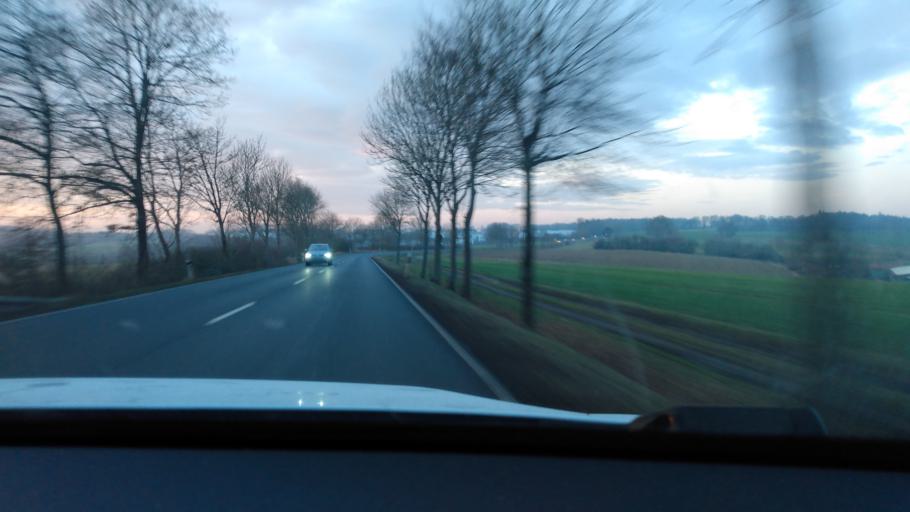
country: DE
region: Rheinland-Pfalz
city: Kircheib
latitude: 50.7090
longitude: 7.4216
